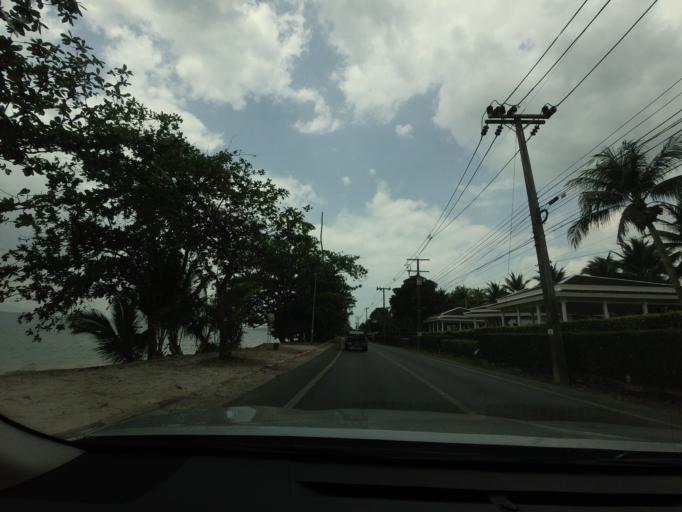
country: TH
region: Phangnga
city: Ban Ao Nang
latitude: 8.0624
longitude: 98.7464
